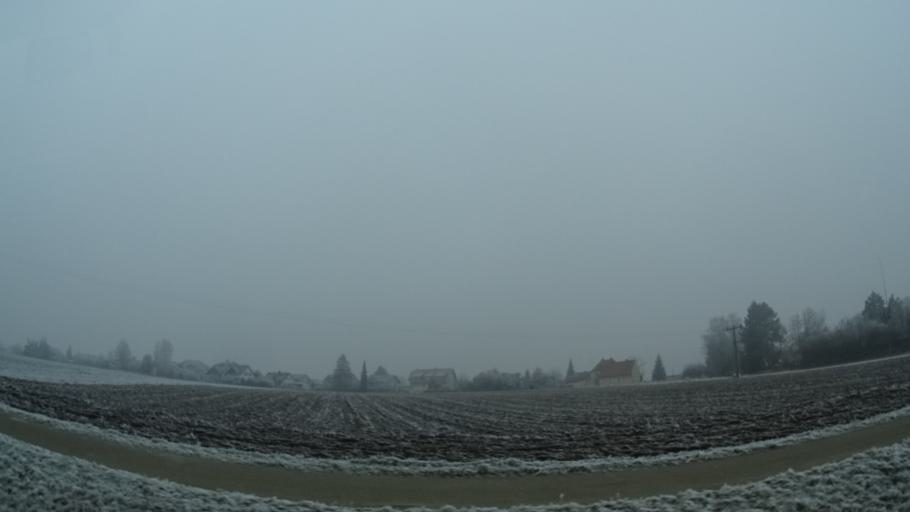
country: DE
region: Bavaria
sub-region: Regierungsbezirk Unterfranken
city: Hassfurt
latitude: 50.0472
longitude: 10.5234
